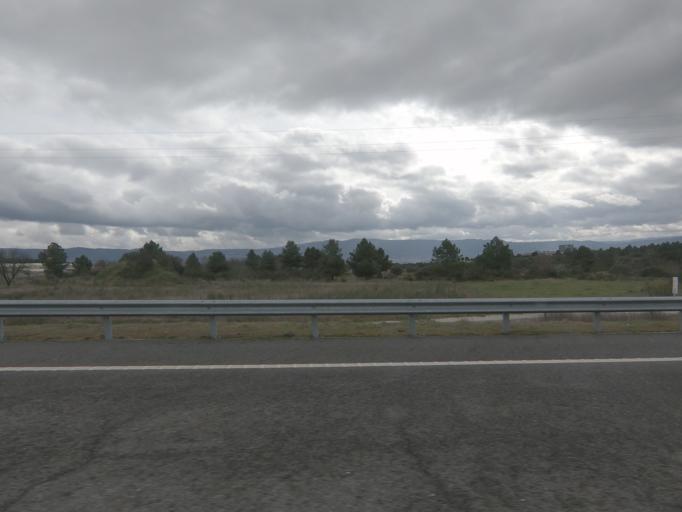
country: PT
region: Vila Real
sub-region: Chaves
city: Chaves
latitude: 41.7692
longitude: -7.4895
